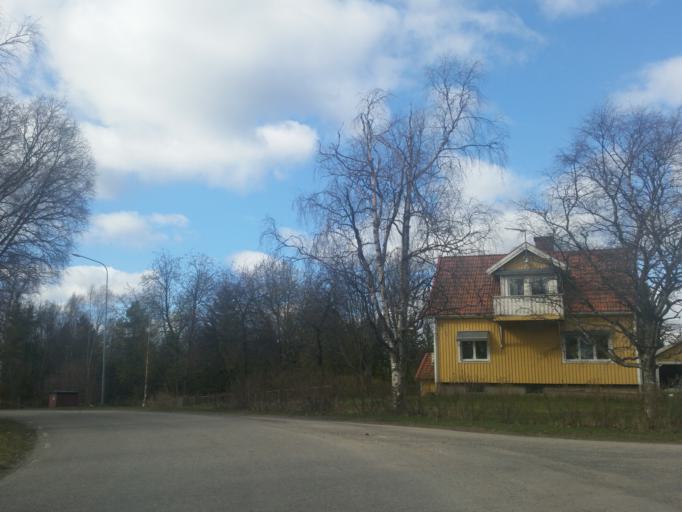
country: SE
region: Vaesterbotten
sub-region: Robertsfors Kommun
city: Robertsfors
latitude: 64.0447
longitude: 20.8587
